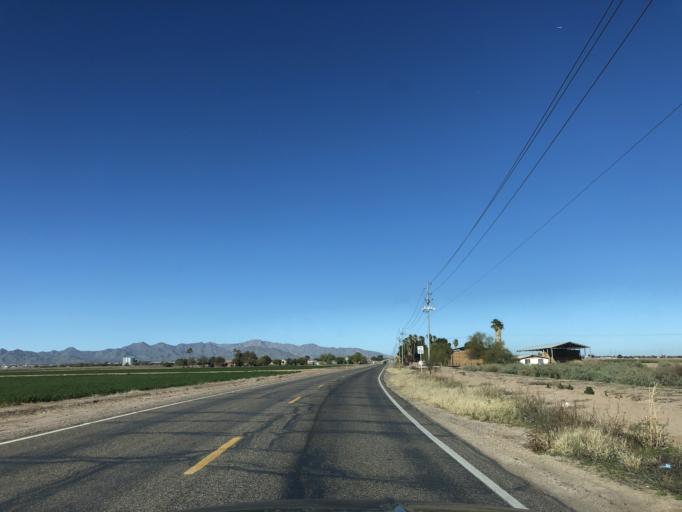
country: US
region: Arizona
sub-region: Maricopa County
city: Buckeye
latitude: 33.3792
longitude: -112.5041
